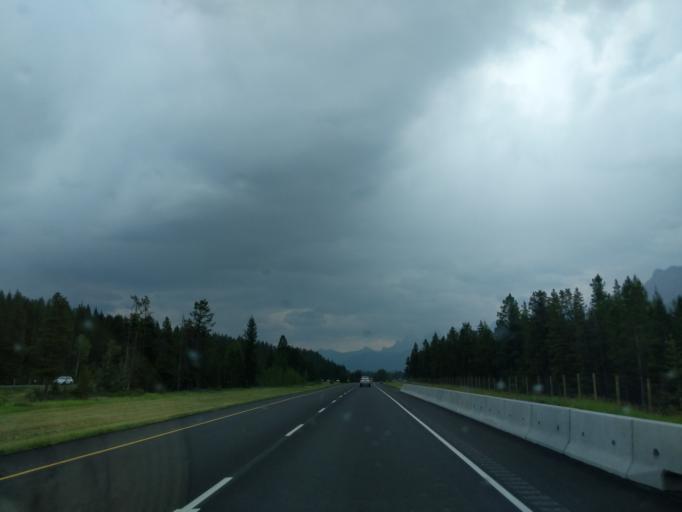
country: CA
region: Alberta
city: Canmore
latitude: 51.1586
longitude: -115.4384
